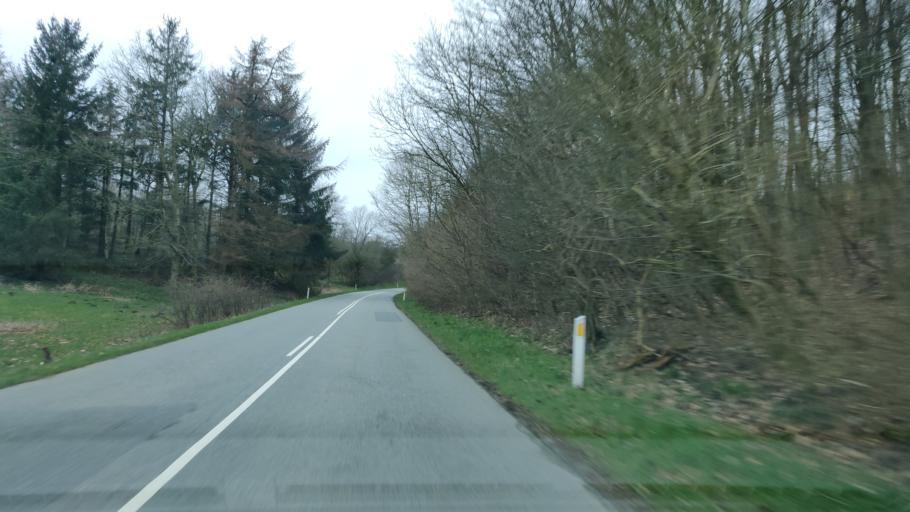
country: DK
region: Central Jutland
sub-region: Skive Kommune
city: Hojslev
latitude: 56.5744
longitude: 9.2340
